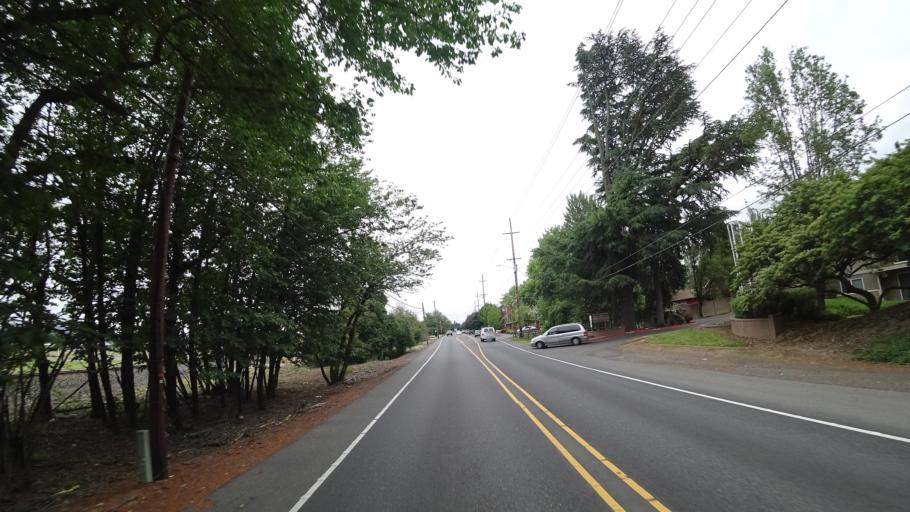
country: US
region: Oregon
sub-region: Multnomah County
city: Fairview
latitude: 45.5515
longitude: -122.5052
